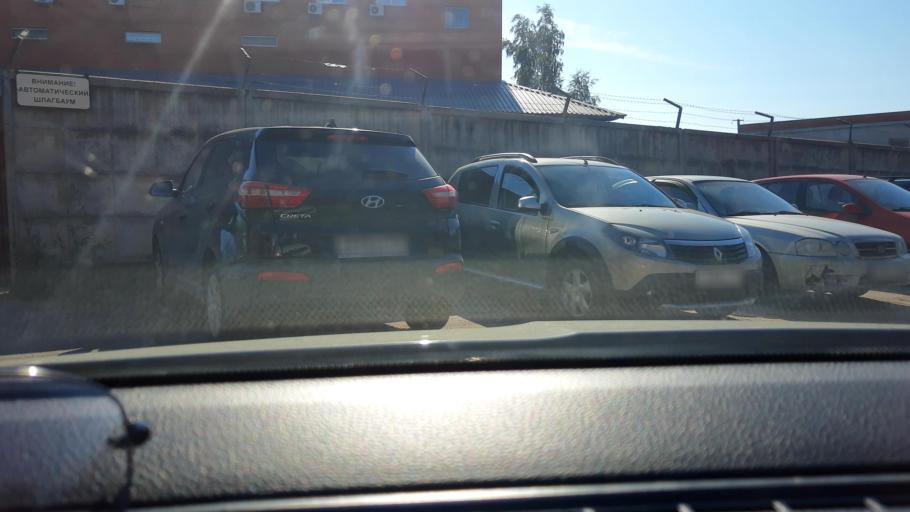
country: RU
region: Moskovskaya
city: Arkhangel'skoye
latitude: 55.8023
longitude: 37.3066
